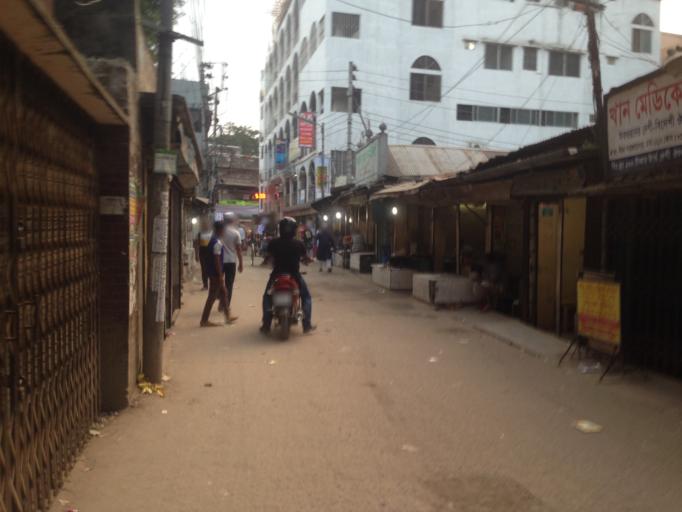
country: BD
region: Dhaka
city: Paltan
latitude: 23.7444
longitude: 90.4242
